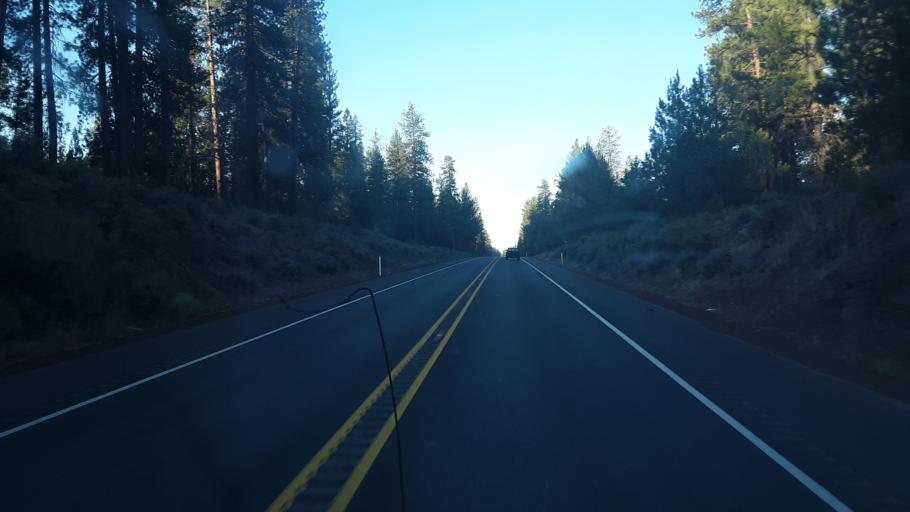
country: US
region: Oregon
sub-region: Deschutes County
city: Three Rivers
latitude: 43.8134
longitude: -121.4313
